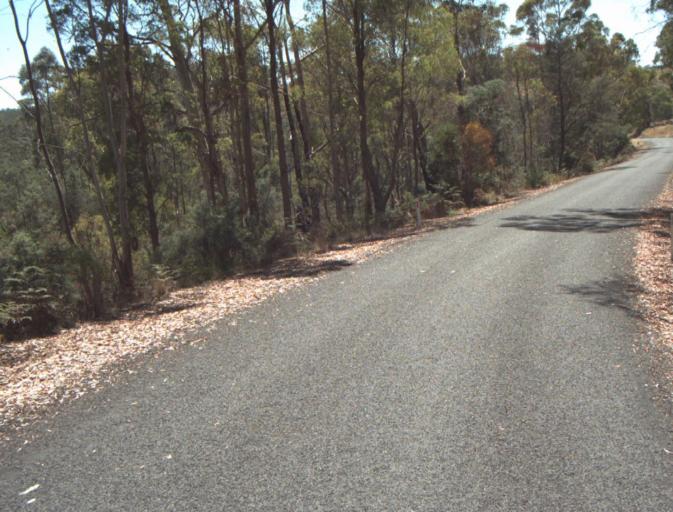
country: AU
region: Tasmania
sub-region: Launceston
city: Newstead
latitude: -41.3685
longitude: 147.3005
